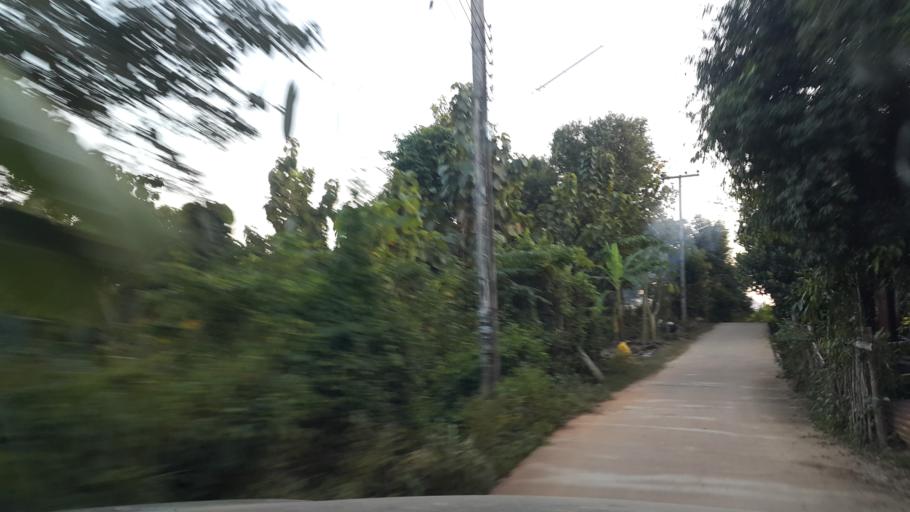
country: TH
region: Phrae
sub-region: Amphoe Wang Chin
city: Wang Chin
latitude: 17.8780
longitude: 99.6234
